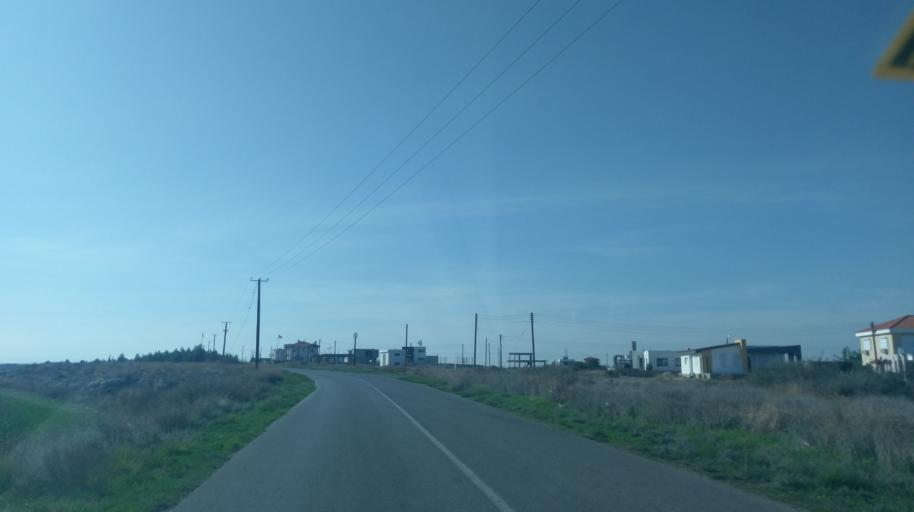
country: CY
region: Larnaka
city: Athienou
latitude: 35.1669
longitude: 33.5320
